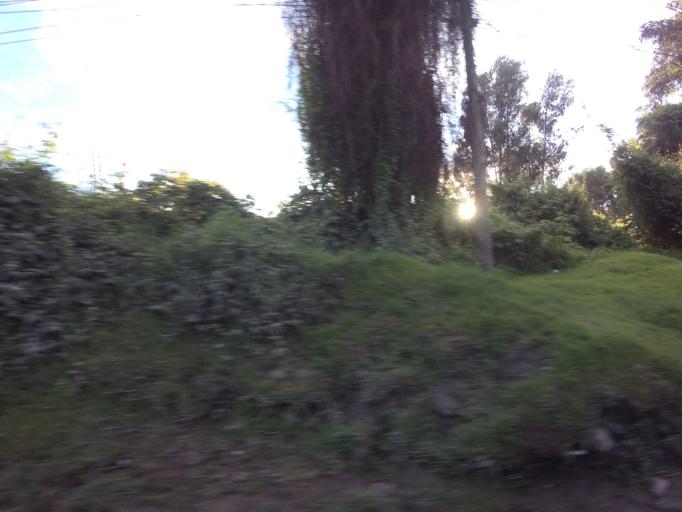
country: CO
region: Cundinamarca
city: Cota
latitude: 4.7808
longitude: -74.0269
